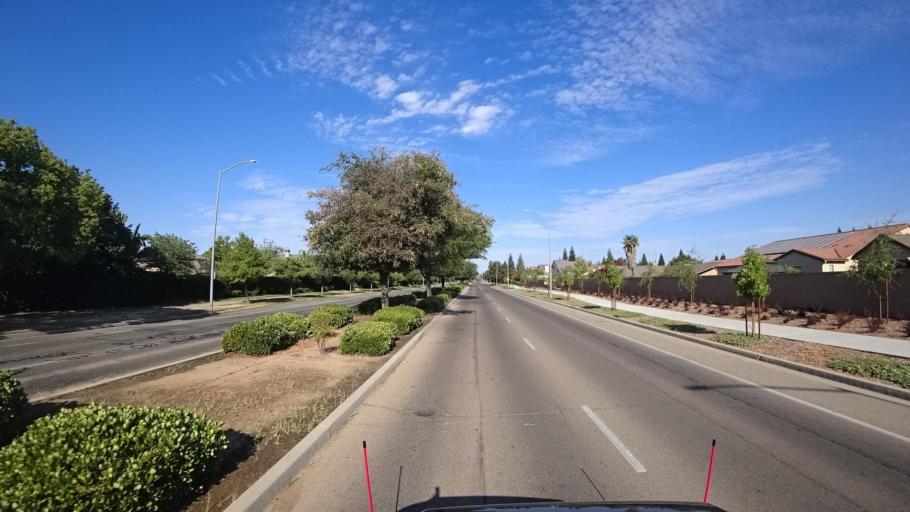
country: US
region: California
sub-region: Fresno County
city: Tarpey Village
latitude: 36.7939
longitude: -119.6569
